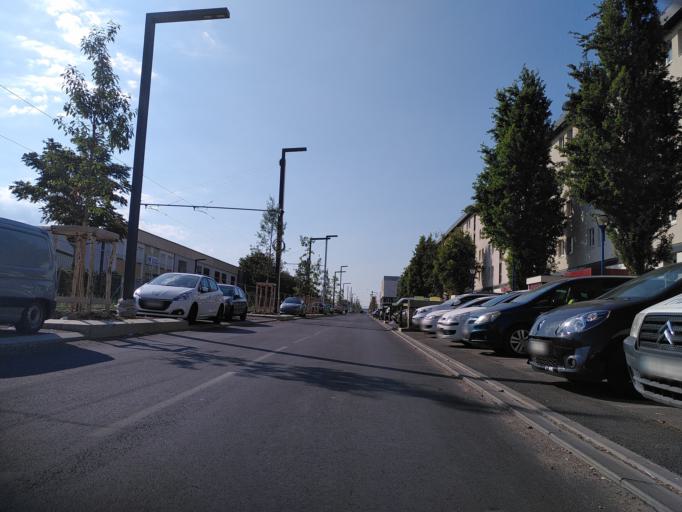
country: FR
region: Ile-de-France
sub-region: Departement du Val-de-Marne
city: Choisy-le-Roi
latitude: 48.7538
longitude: 2.4157
